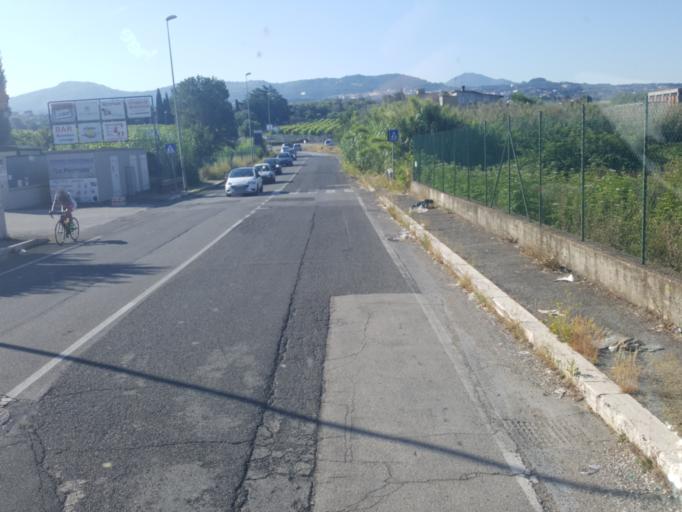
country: IT
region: Latium
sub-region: Citta metropolitana di Roma Capitale
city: Frascati
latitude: 41.8380
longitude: 12.6571
